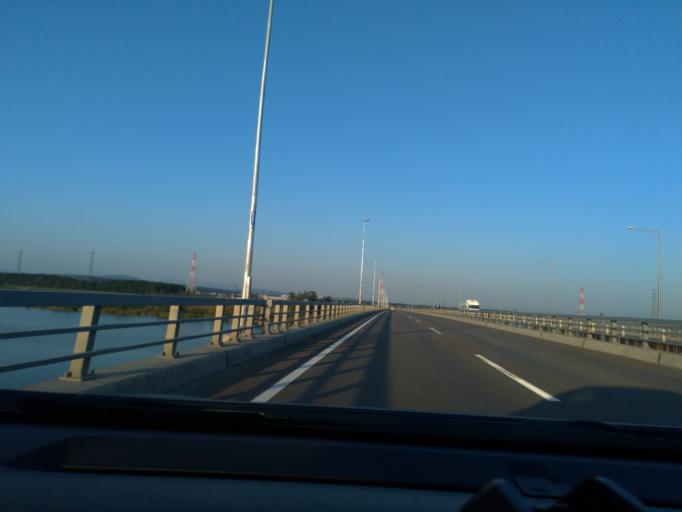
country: JP
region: Hokkaido
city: Ishikari
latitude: 43.1727
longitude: 141.4192
